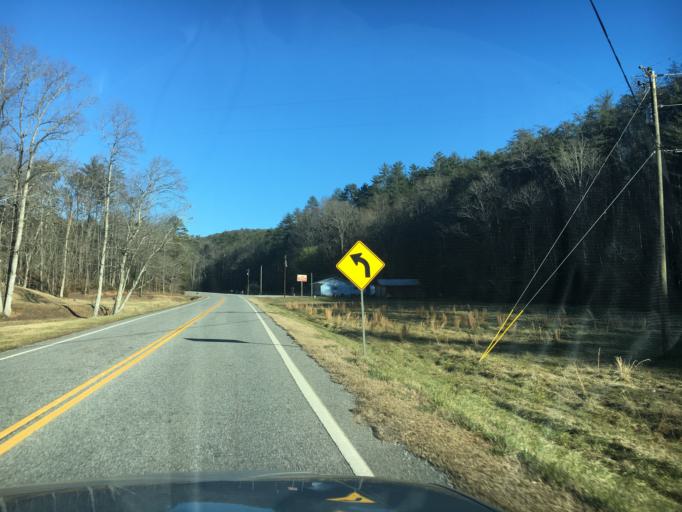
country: US
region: Georgia
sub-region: White County
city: Cleveland
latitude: 34.6608
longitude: -83.8962
